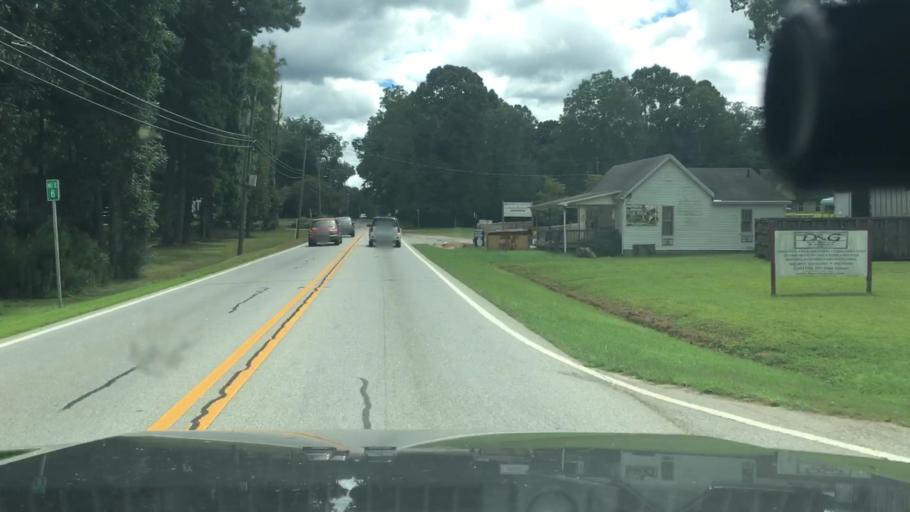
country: US
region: Georgia
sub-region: Coweta County
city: East Newnan
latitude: 33.2899
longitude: -84.7687
